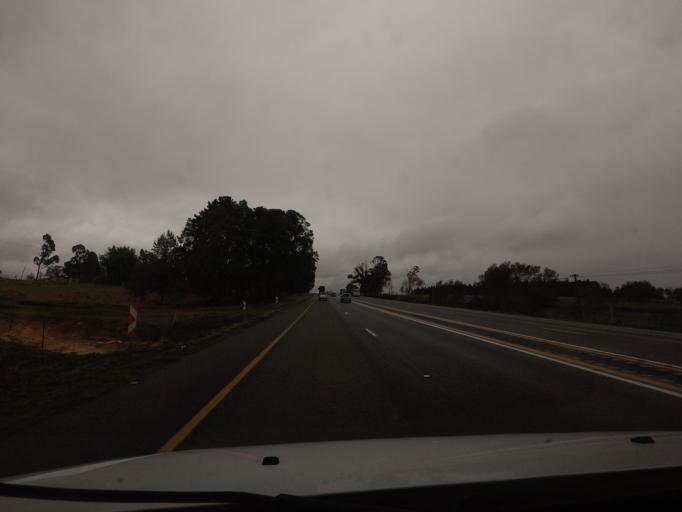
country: ZA
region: Mpumalanga
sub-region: Nkangala District Municipality
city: Belfast
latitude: -25.7527
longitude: 29.9979
